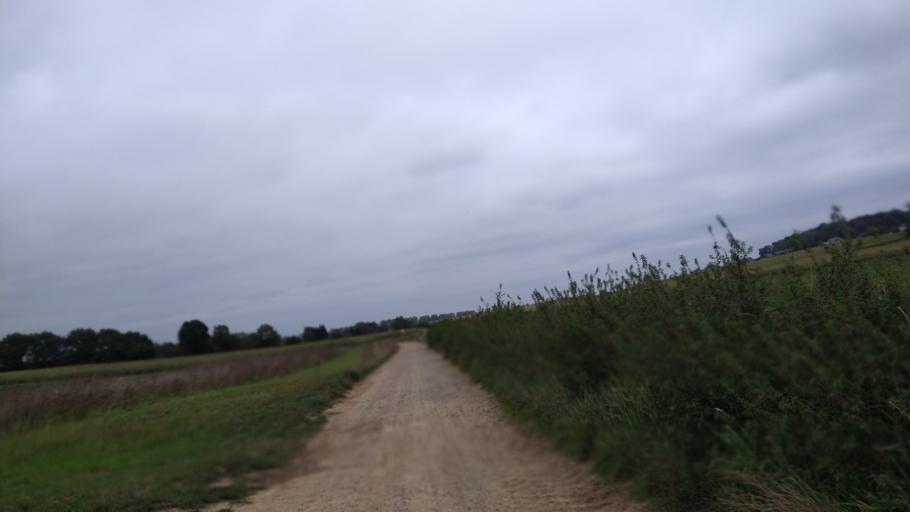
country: BE
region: Flanders
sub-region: Provincie Vlaams-Brabant
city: Kortenberg
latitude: 50.8556
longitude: 4.5757
